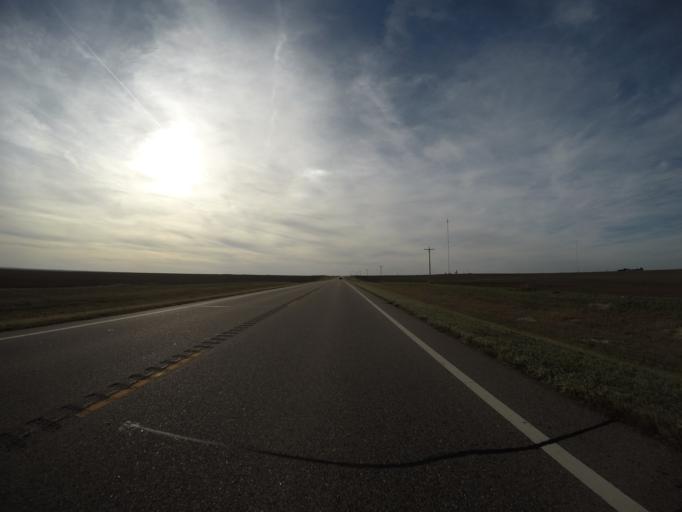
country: US
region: Kansas
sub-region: Cheyenne County
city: Saint Francis
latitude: 39.7566
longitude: -101.6868
